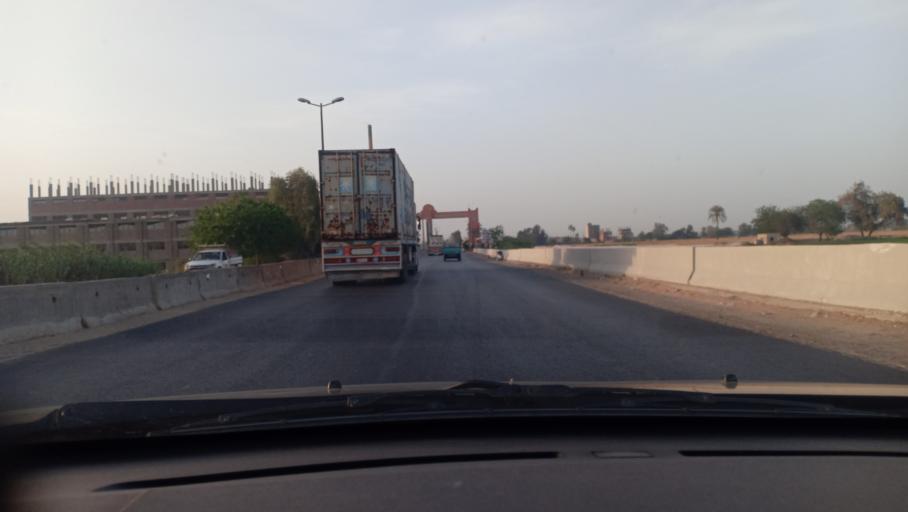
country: EG
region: Muhafazat al Gharbiyah
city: Zifta
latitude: 30.6023
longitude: 31.2746
